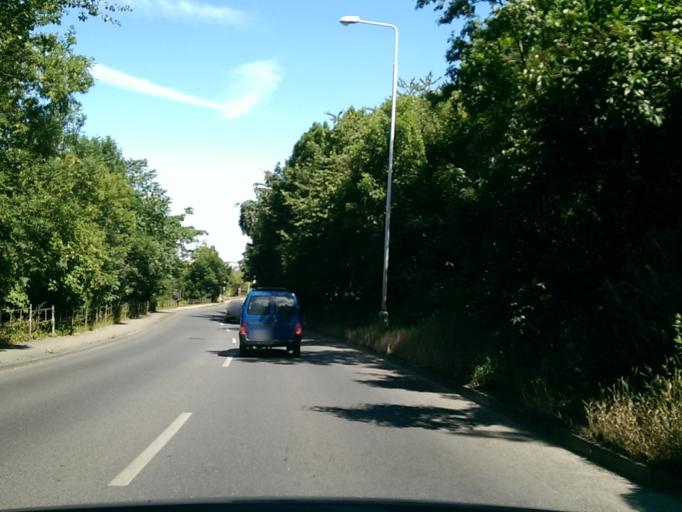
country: CZ
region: Praha
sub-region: Praha 8
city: Liben
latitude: 50.0934
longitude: 14.4730
